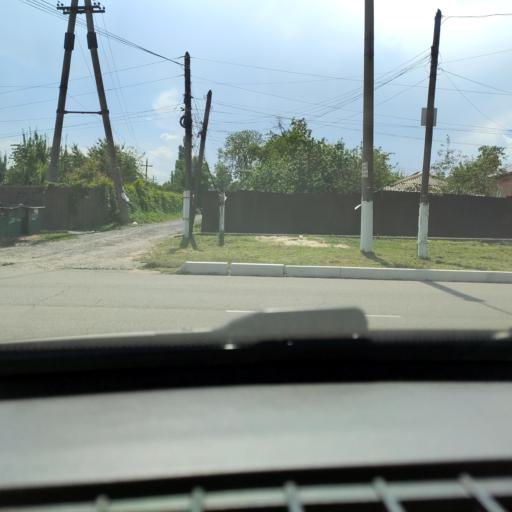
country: RU
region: Voronezj
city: Semiluki
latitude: 51.6876
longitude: 39.0251
